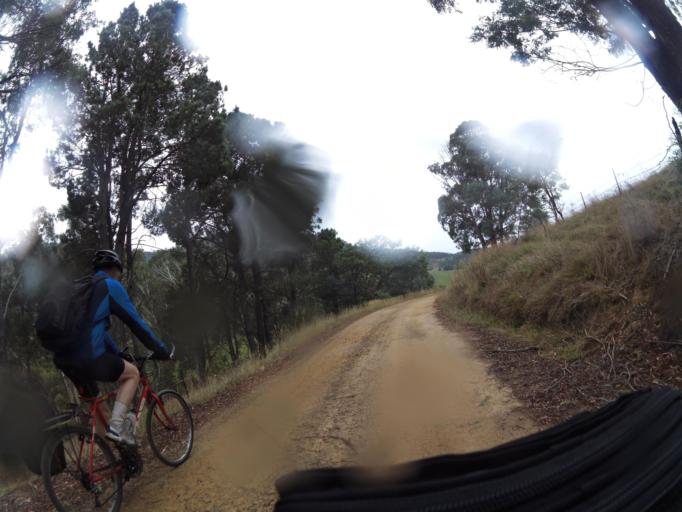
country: AU
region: New South Wales
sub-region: Greater Hume Shire
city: Holbrook
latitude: -36.2369
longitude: 147.6158
